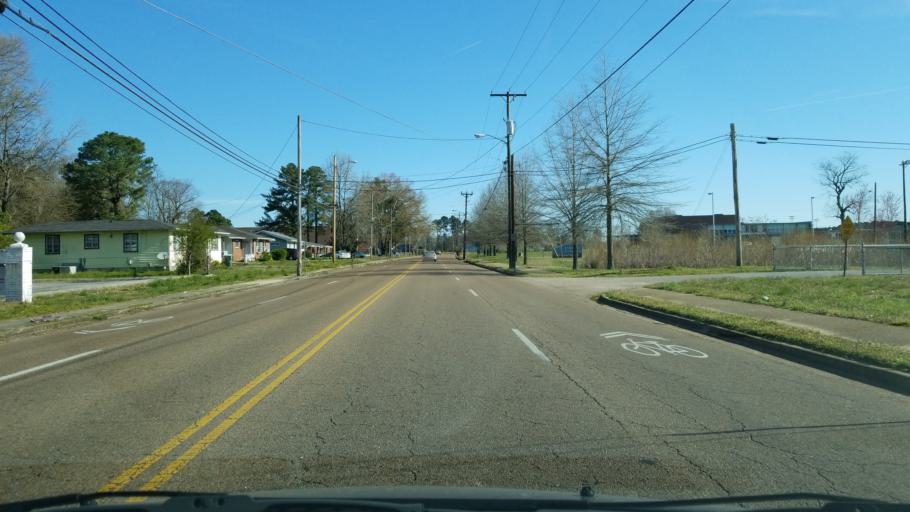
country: US
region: Tennessee
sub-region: Hamilton County
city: East Ridge
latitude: 35.0263
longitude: -85.2210
